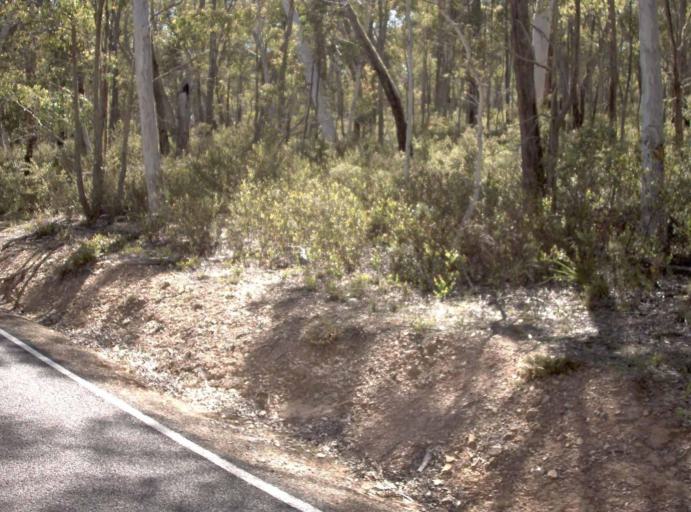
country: AU
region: New South Wales
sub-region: Bombala
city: Bombala
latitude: -37.1375
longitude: 148.7356
